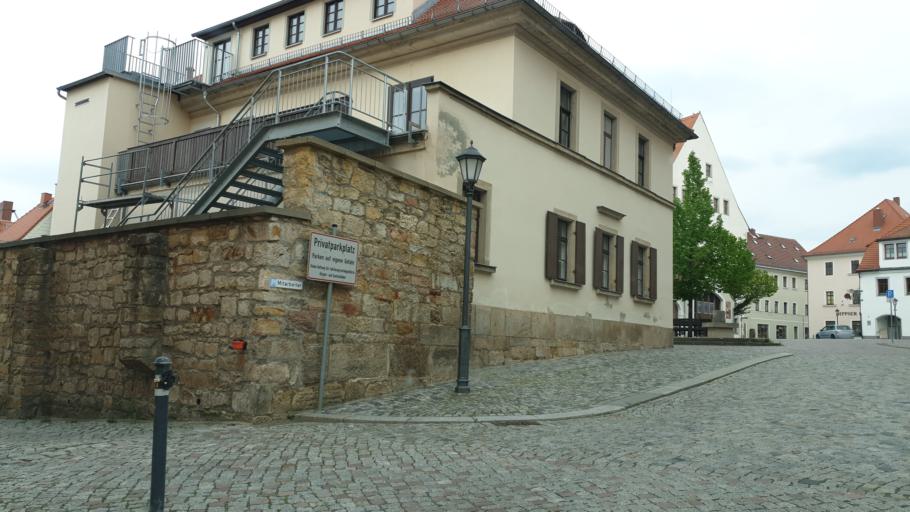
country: DE
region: Saxony
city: Dippoldiswalde
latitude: 50.8959
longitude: 13.6665
